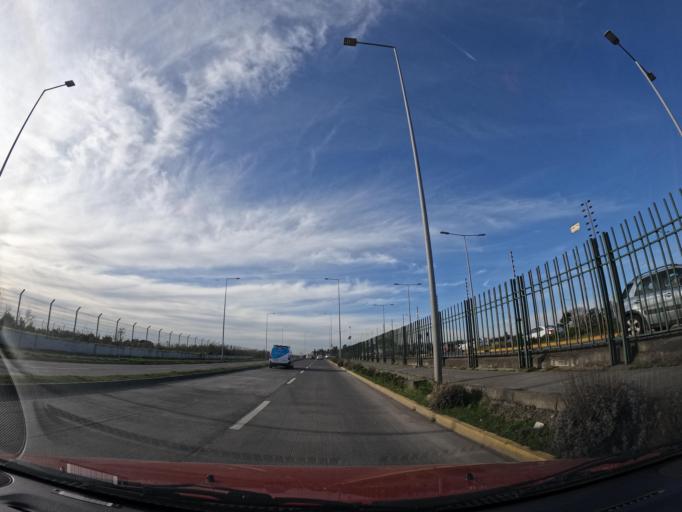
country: CL
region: Biobio
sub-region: Provincia de Concepcion
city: Concepcion
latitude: -36.7893
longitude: -73.0686
